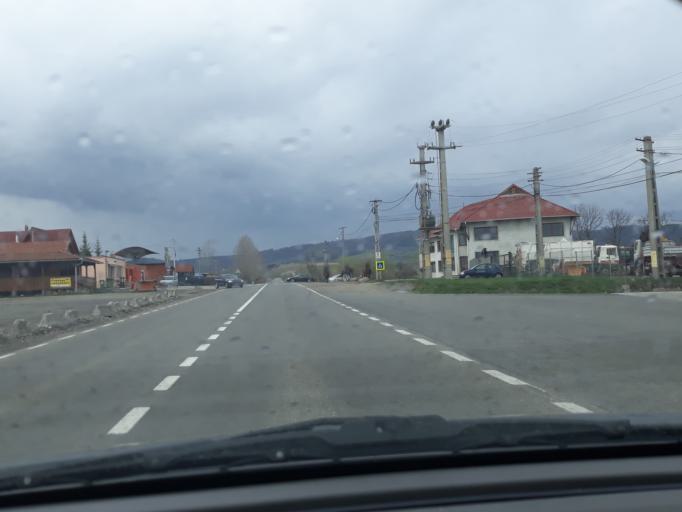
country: RO
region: Harghita
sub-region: Comuna Lupeni
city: Lupeni
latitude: 46.3830
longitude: 25.2188
